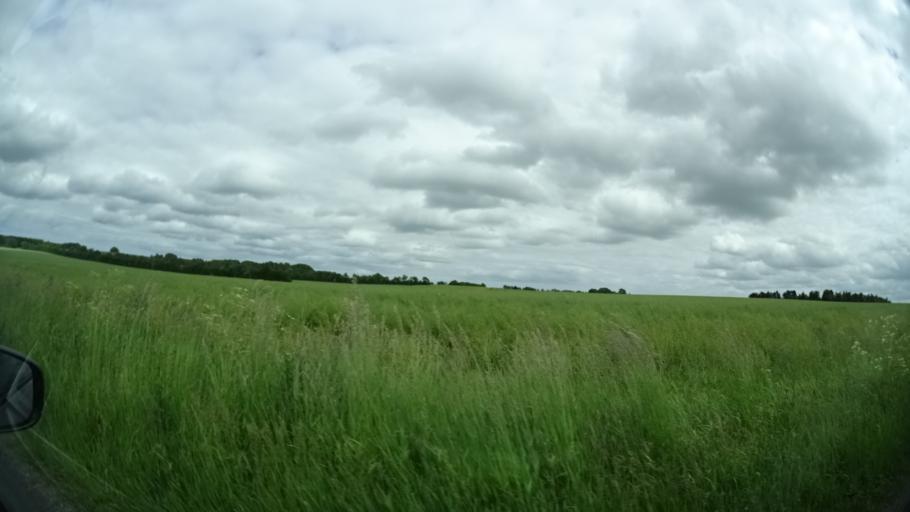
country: DK
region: Central Jutland
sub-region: Norddjurs Kommune
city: Grenaa
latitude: 56.4530
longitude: 10.7120
